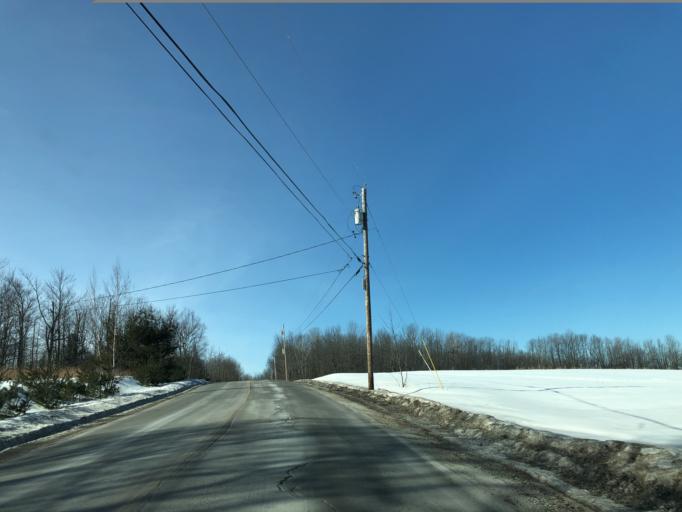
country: US
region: Maine
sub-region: Androscoggin County
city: Minot
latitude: 44.1331
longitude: -70.3083
